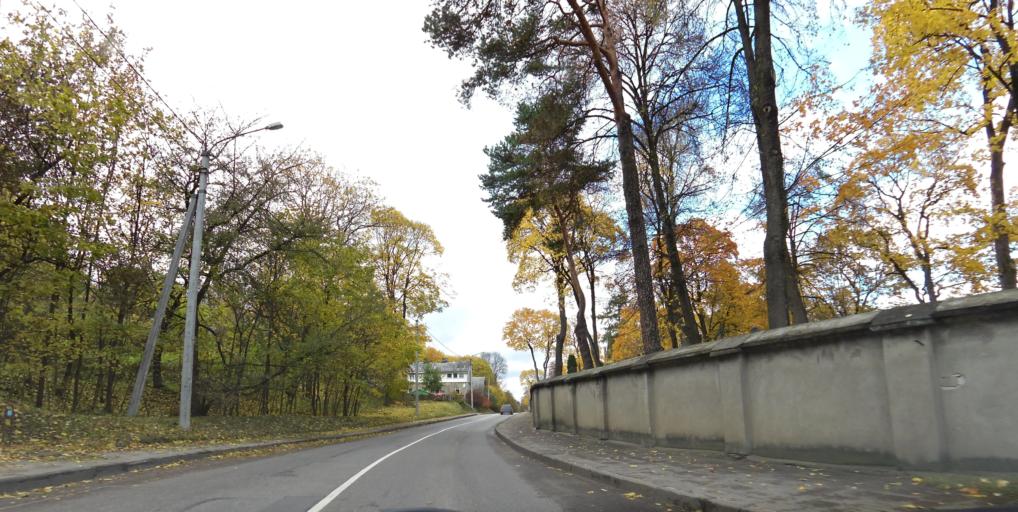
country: LT
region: Vilnius County
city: Rasos
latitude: 54.6674
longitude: 25.3040
